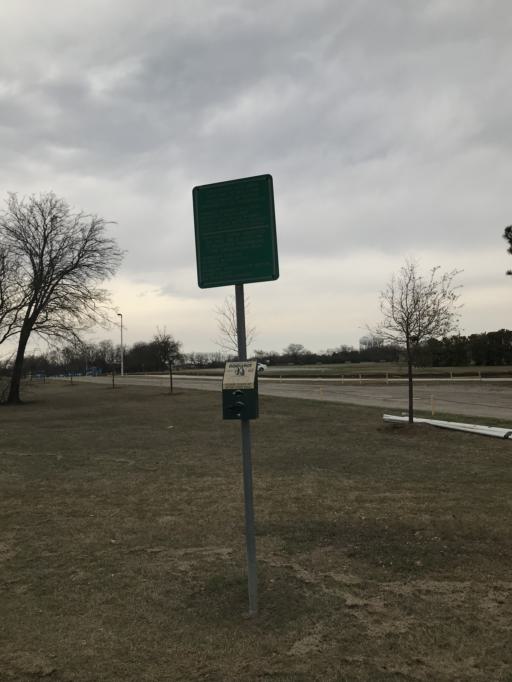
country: US
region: Texas
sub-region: Denton County
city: Denton
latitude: 33.2421
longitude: -97.1445
